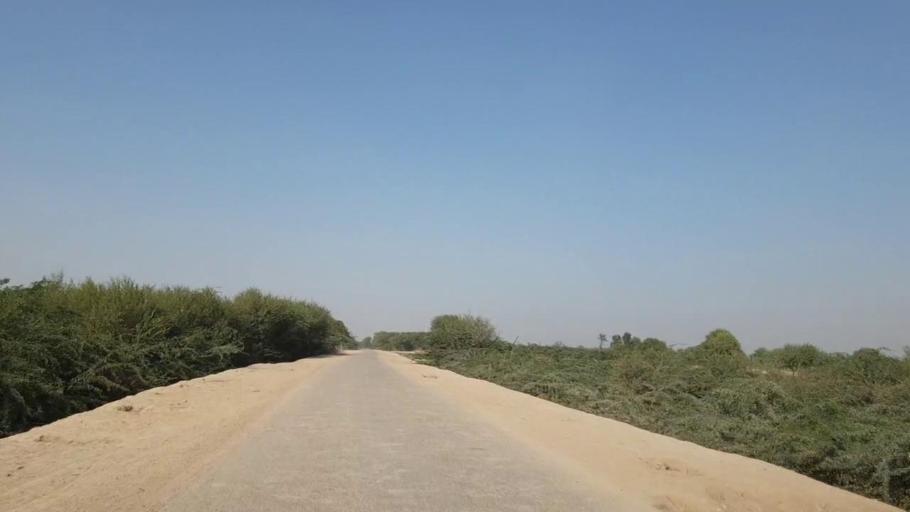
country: PK
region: Sindh
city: Digri
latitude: 24.9912
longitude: 69.1086
